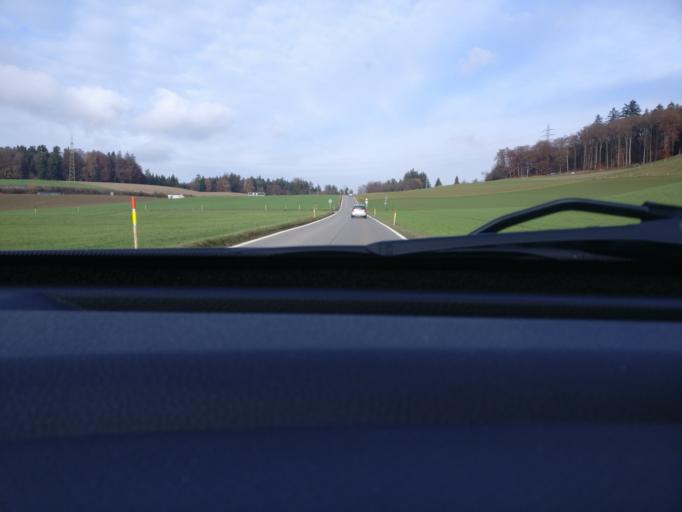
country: CH
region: Bern
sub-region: Bern-Mittelland District
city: Bolligen
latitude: 46.9878
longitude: 7.4814
